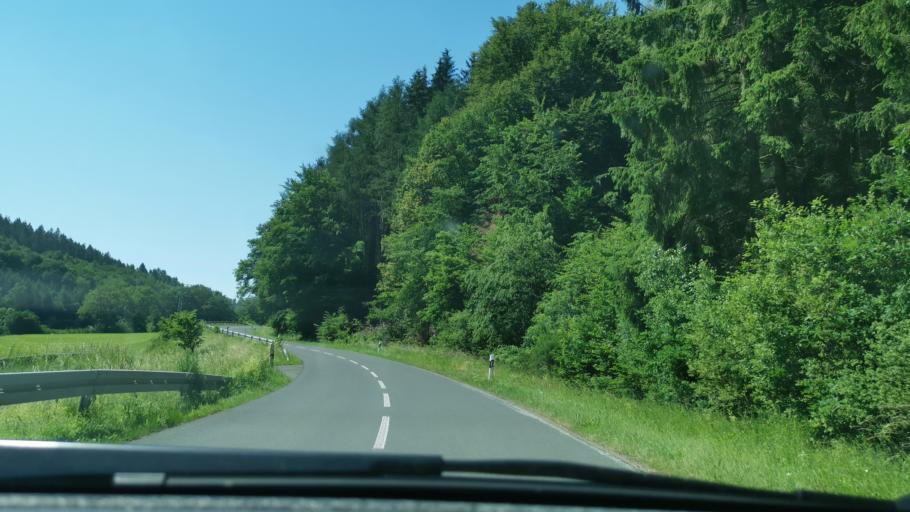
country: DE
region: Hesse
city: Spangenberg
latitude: 51.1219
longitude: 9.7071
